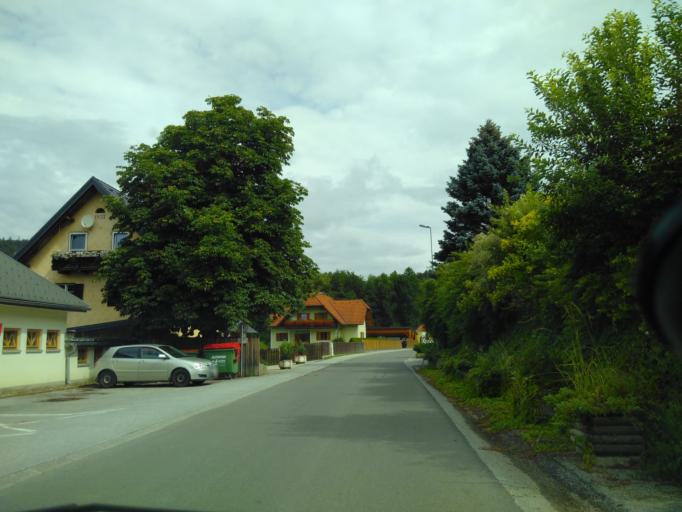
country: AT
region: Styria
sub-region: Politischer Bezirk Graz-Umgebung
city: Semriach
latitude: 47.2212
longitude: 15.3987
